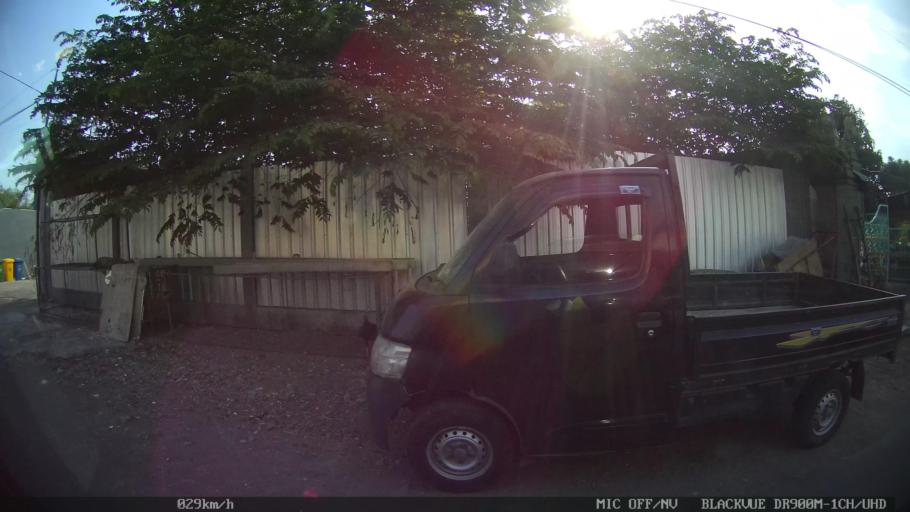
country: ID
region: Daerah Istimewa Yogyakarta
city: Yogyakarta
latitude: -7.8171
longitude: 110.3784
